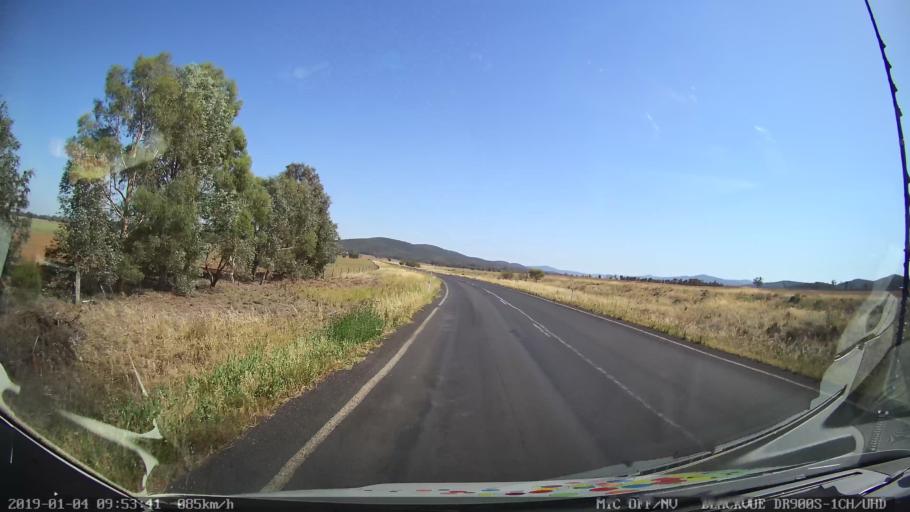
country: AU
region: New South Wales
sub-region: Cabonne
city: Canowindra
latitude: -33.5493
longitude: 148.4196
